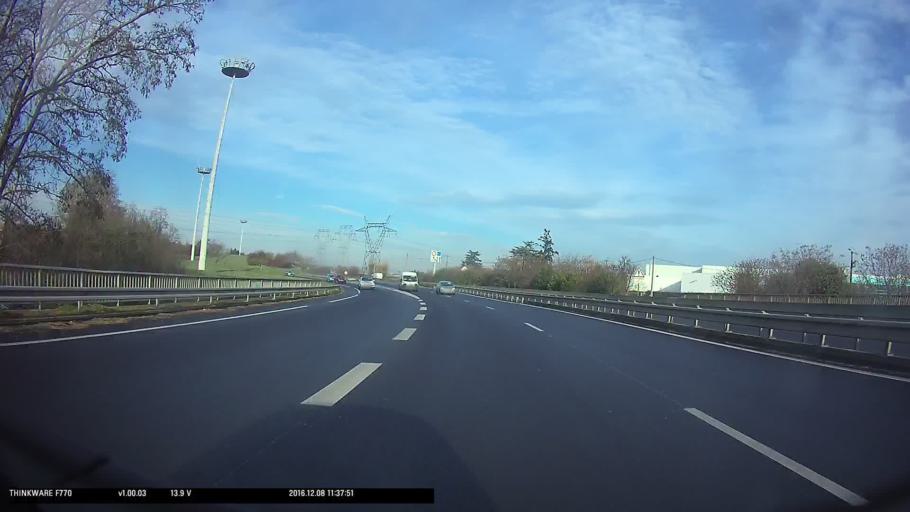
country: FR
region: Ile-de-France
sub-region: Departement du Val-d'Oise
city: Pontoise
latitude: 49.0648
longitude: 2.0866
